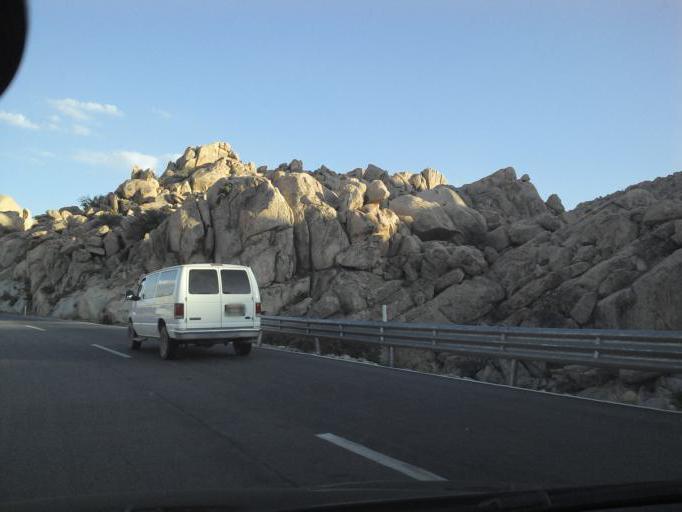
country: MX
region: Baja California
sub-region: Tecate
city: Cereso del Hongo
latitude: 32.5782
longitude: -116.0272
